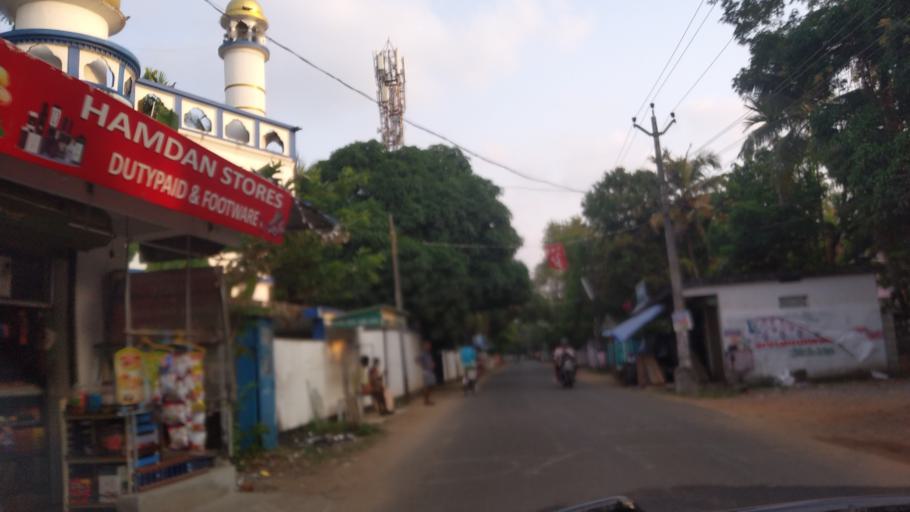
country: IN
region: Kerala
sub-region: Thrissur District
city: Thanniyam
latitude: 10.3521
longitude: 76.1126
